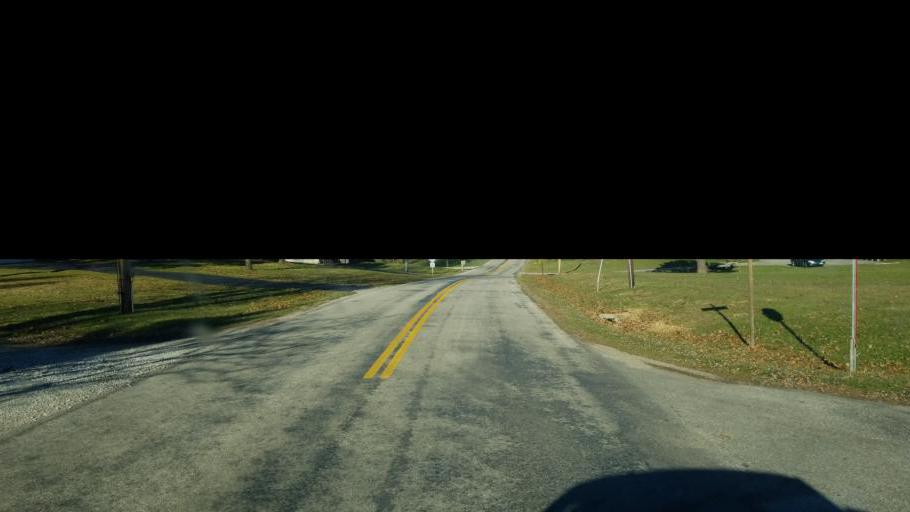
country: US
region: Ohio
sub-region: Ashland County
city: Ashland
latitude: 40.8369
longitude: -82.3621
